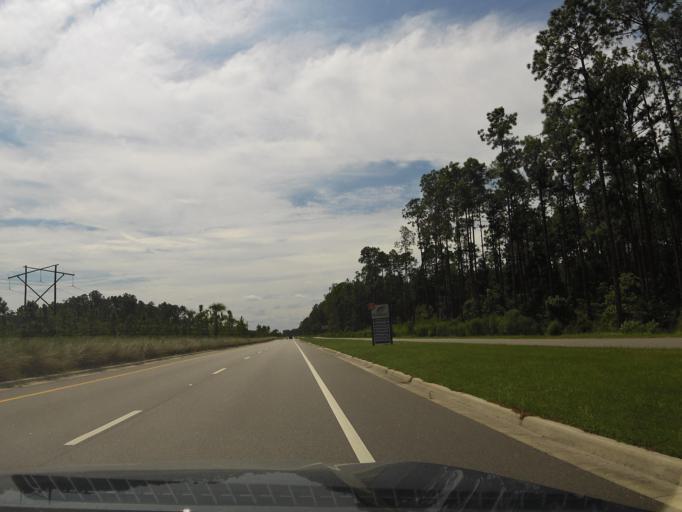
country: US
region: Florida
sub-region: Saint Johns County
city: Fruit Cove
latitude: 30.0538
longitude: -81.5302
